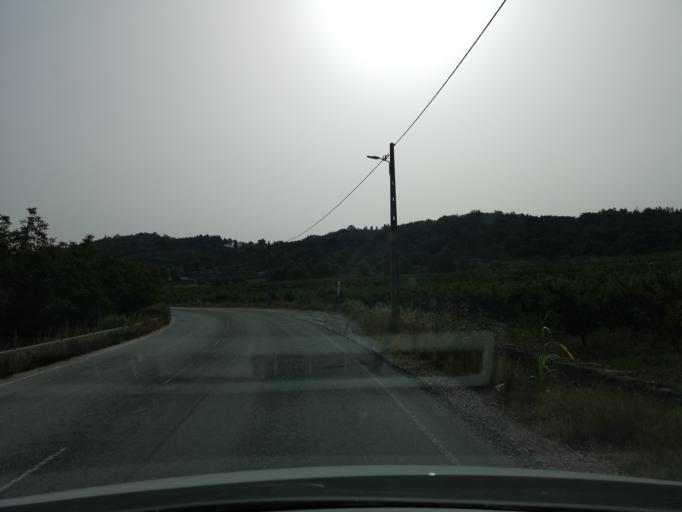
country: PT
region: Castelo Branco
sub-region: Belmonte
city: Belmonte
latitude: 40.3657
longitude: -7.3367
